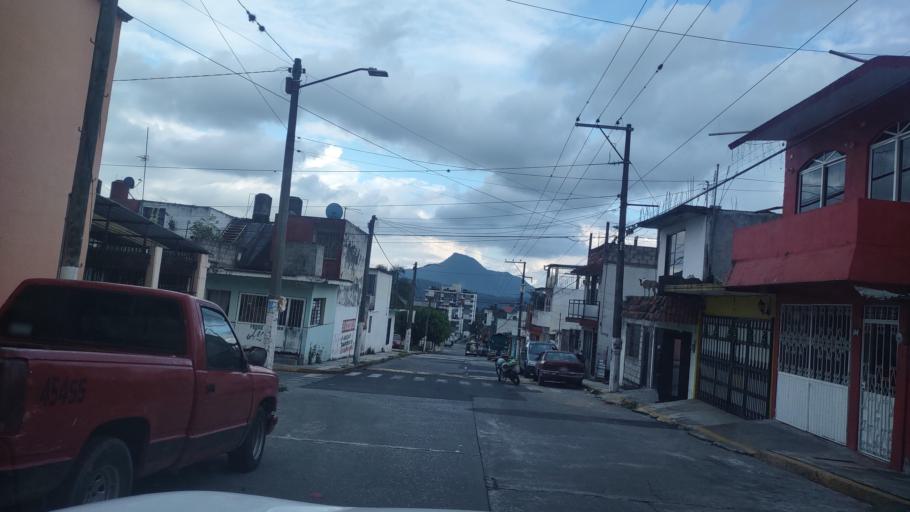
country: MX
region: Veracruz
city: Ixtac Zoquitlan
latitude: 18.8838
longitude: -97.0646
